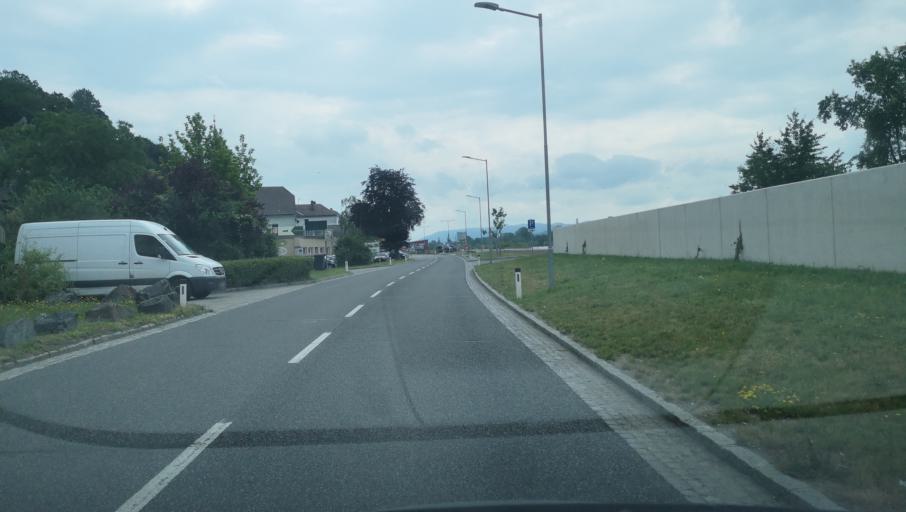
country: AT
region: Lower Austria
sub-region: Politischer Bezirk Melk
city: Marbach an der Donau
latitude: 48.2143
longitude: 15.1459
